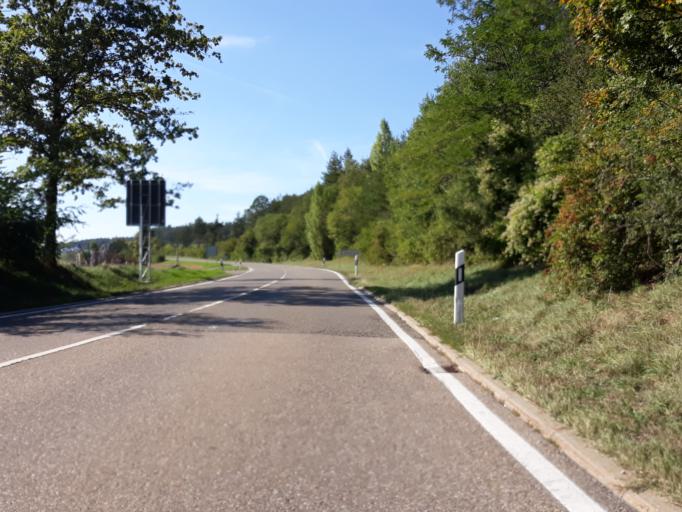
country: DE
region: Baden-Wuerttemberg
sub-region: Regierungsbezirk Stuttgart
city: Weil der Stadt
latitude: 48.7250
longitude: 8.8748
